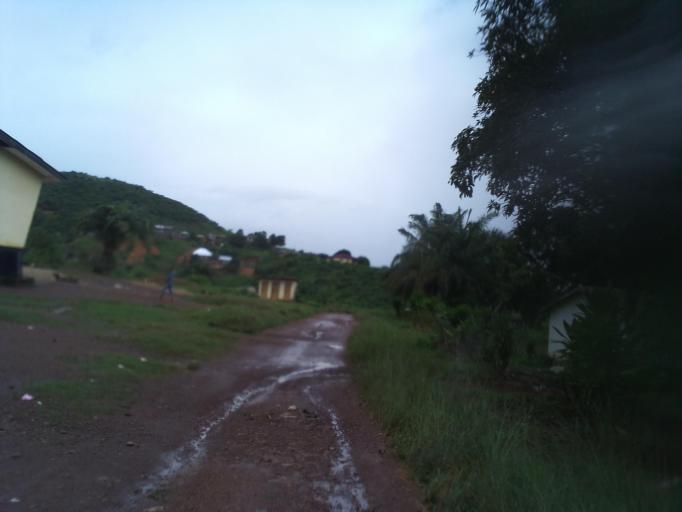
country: SL
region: Eastern Province
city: Kenema
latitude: 7.8528
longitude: -11.1951
